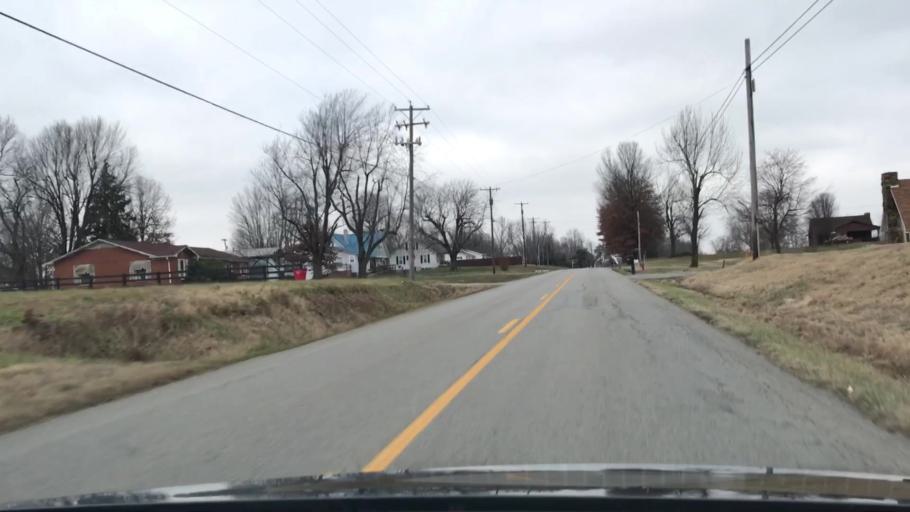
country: US
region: Kentucky
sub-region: Muhlenberg County
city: Morehead
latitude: 37.3888
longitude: -87.2533
